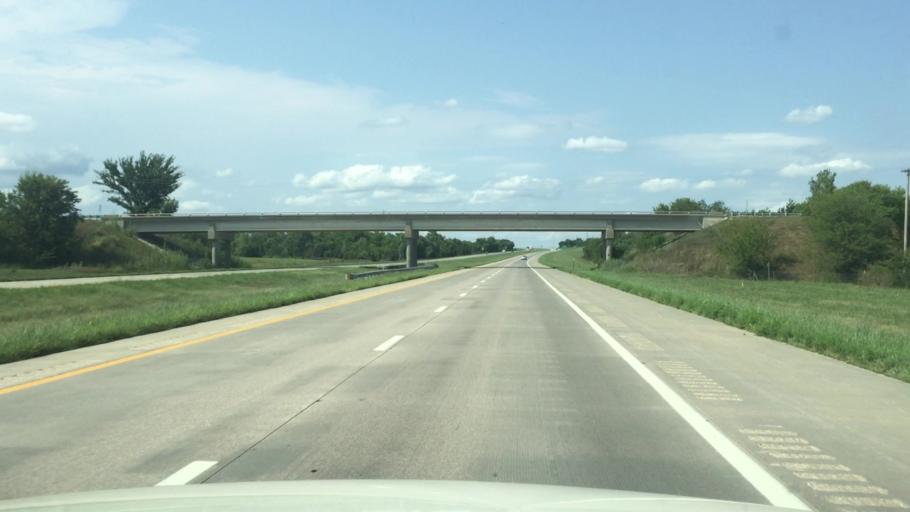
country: US
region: Kansas
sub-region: Linn County
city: La Cygne
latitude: 38.4607
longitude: -94.6863
